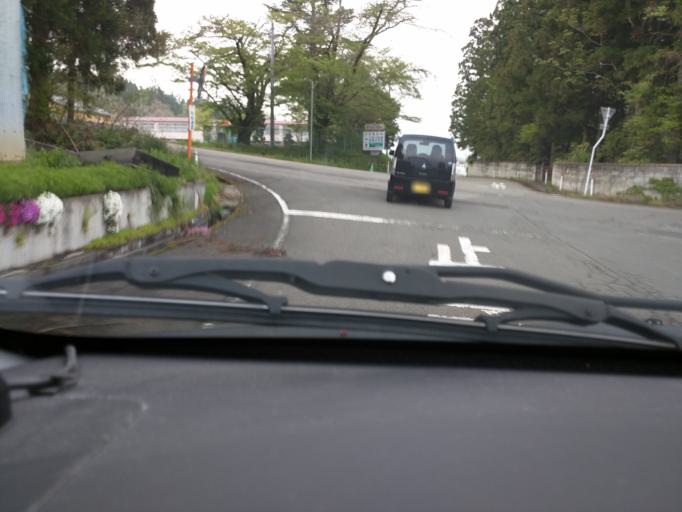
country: JP
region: Fukushima
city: Kitakata
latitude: 37.5020
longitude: 139.8222
